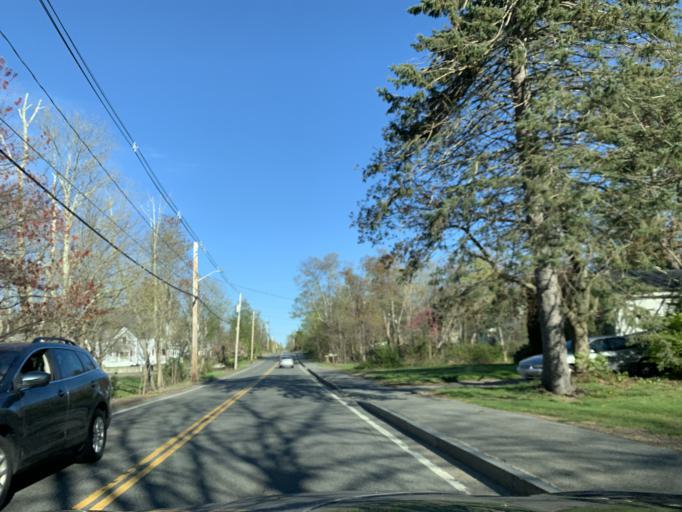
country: US
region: Massachusetts
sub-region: Norfolk County
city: Stoughton
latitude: 42.1300
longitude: -71.1231
